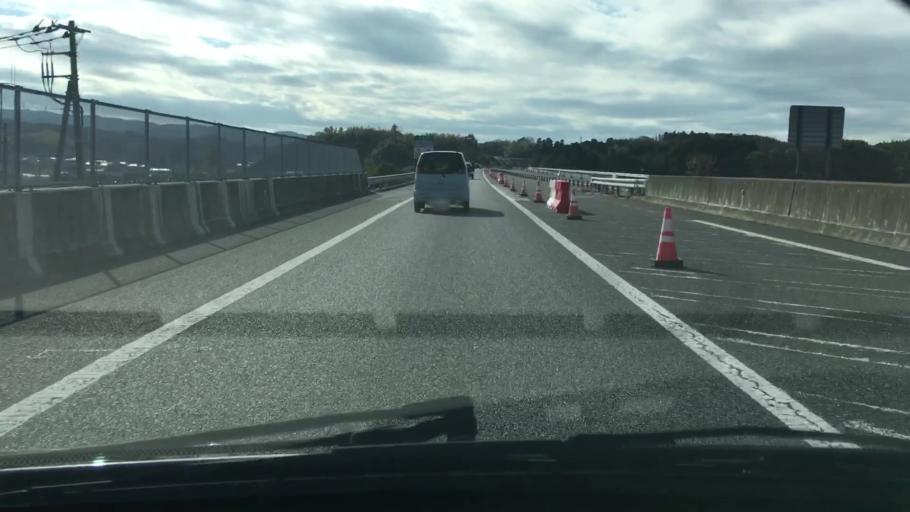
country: JP
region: Chiba
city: Kimitsu
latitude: 35.3082
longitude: 139.9423
